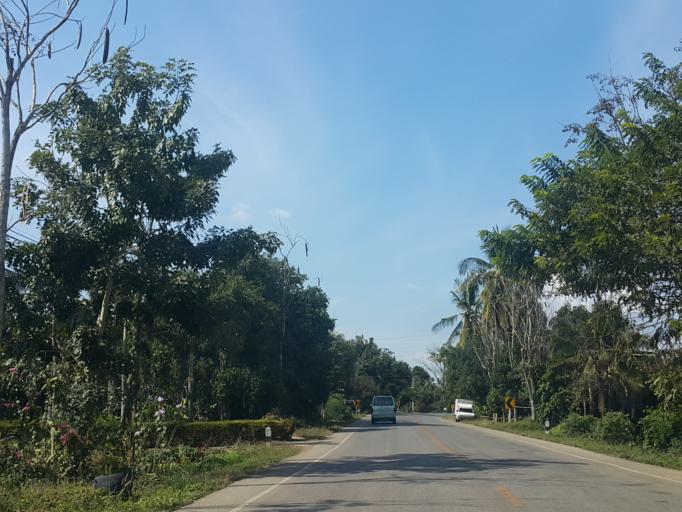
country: TH
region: Sukhothai
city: Sawankhalok
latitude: 17.2677
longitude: 99.8328
